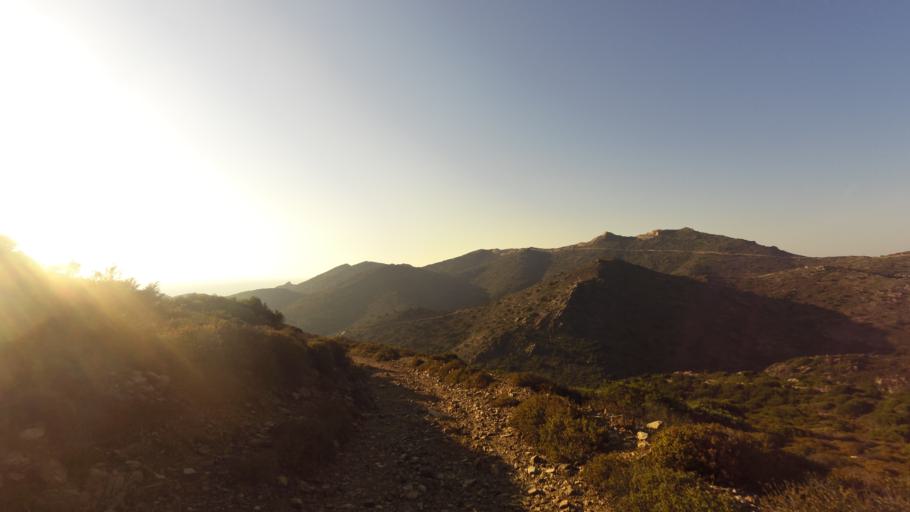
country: GR
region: South Aegean
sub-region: Nomos Kykladon
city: Antiparos
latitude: 37.0001
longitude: 25.0376
